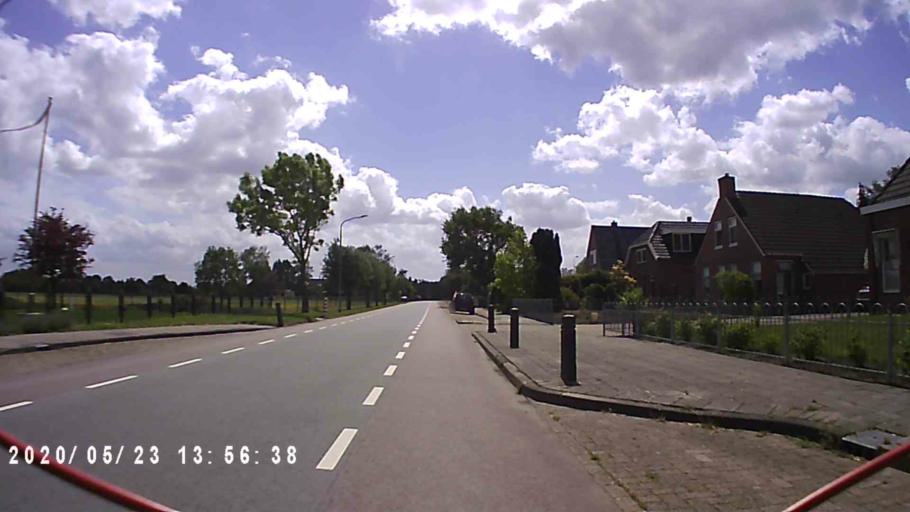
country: NL
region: Groningen
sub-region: Gemeente  Oldambt
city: Winschoten
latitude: 53.2687
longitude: 7.0277
